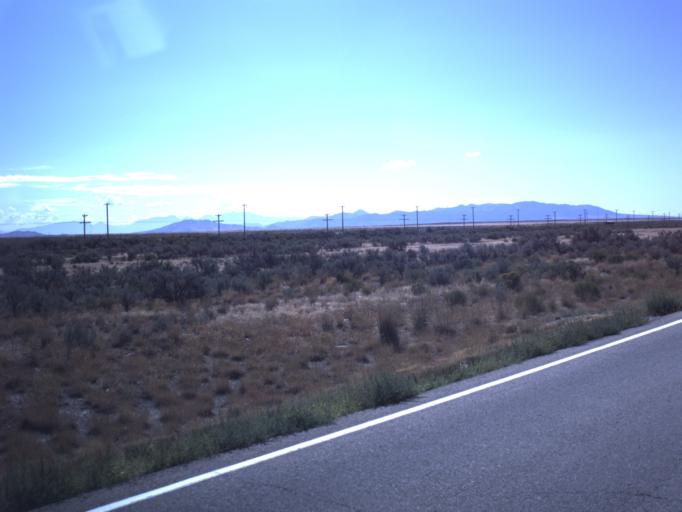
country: US
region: Utah
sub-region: Tooele County
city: Tooele
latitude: 40.2714
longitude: -112.3977
